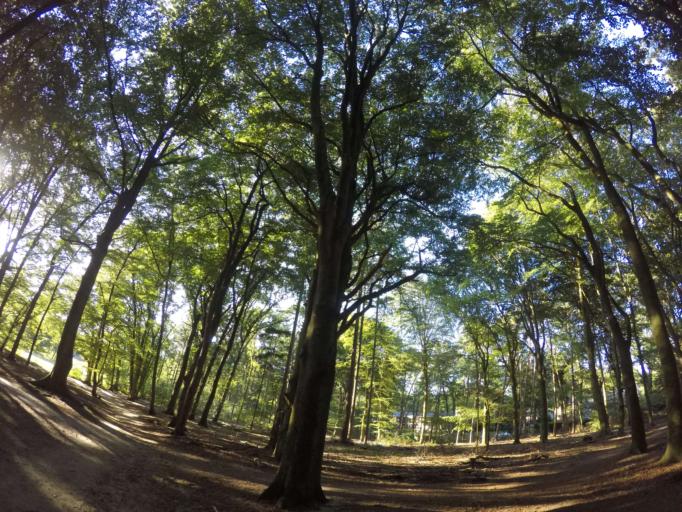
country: NL
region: Gelderland
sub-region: Gemeente Arnhem
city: Gulden Bodem
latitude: 52.0025
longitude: 5.8994
